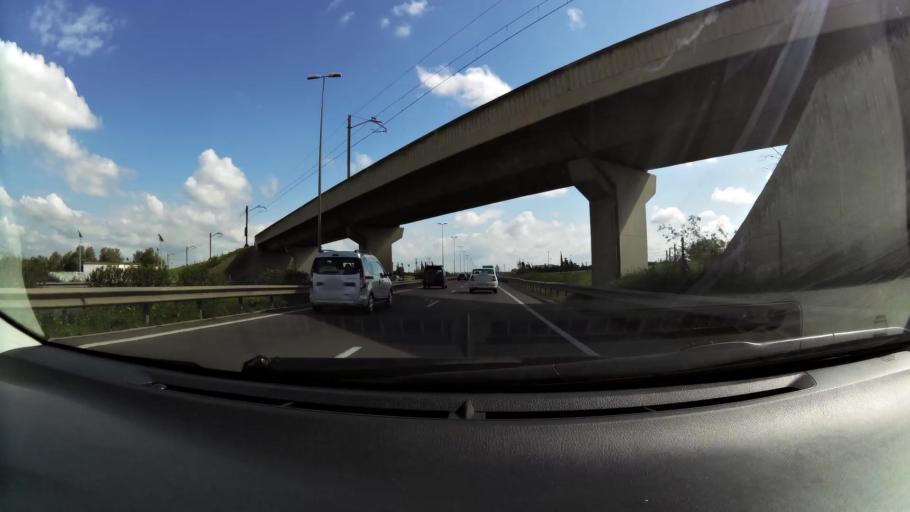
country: MA
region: Chaouia-Ouardigha
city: Nouaseur
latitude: 33.3971
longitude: -7.6208
